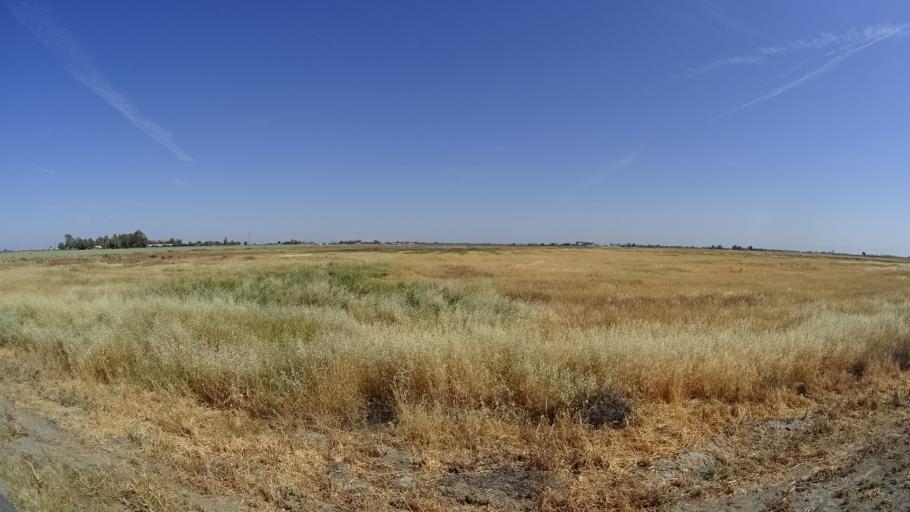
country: US
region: California
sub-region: Kings County
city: Stratford
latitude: 36.2113
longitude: -119.7746
